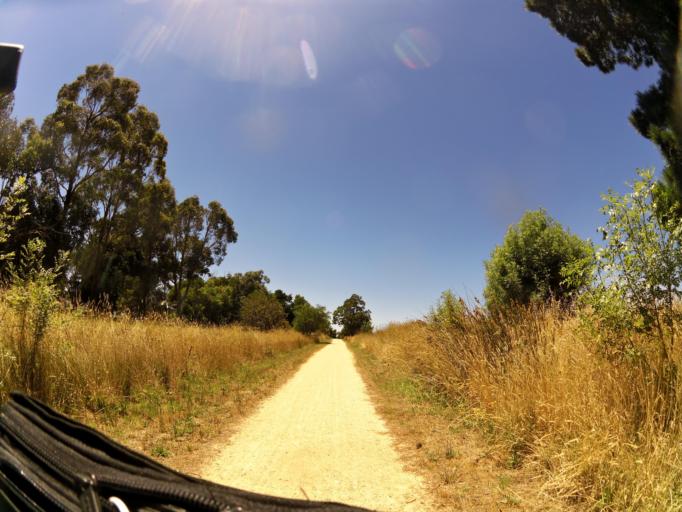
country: AU
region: Victoria
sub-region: Ballarat North
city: Newington
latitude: -37.5371
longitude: 143.7765
